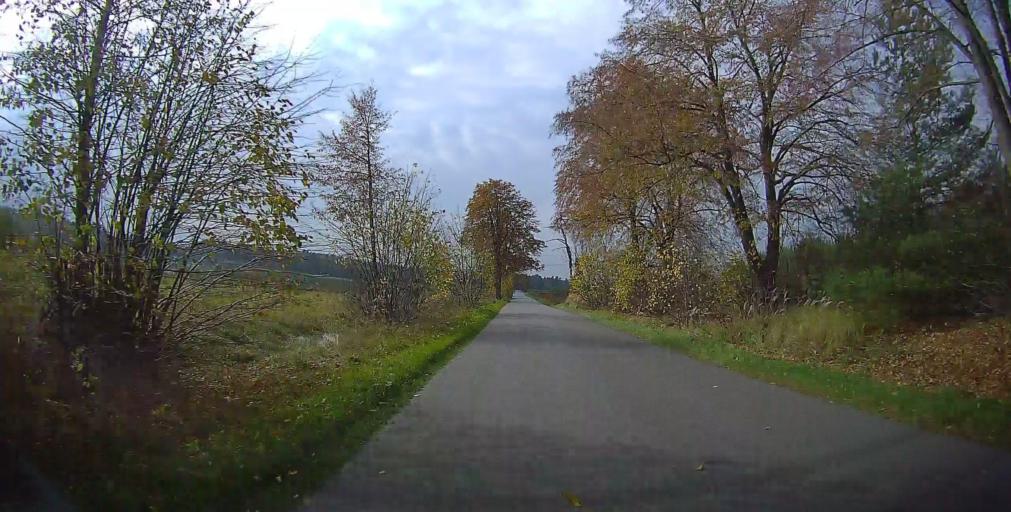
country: PL
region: Masovian Voivodeship
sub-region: Powiat bialobrzeski
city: Wysmierzyce
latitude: 51.6503
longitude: 20.7662
